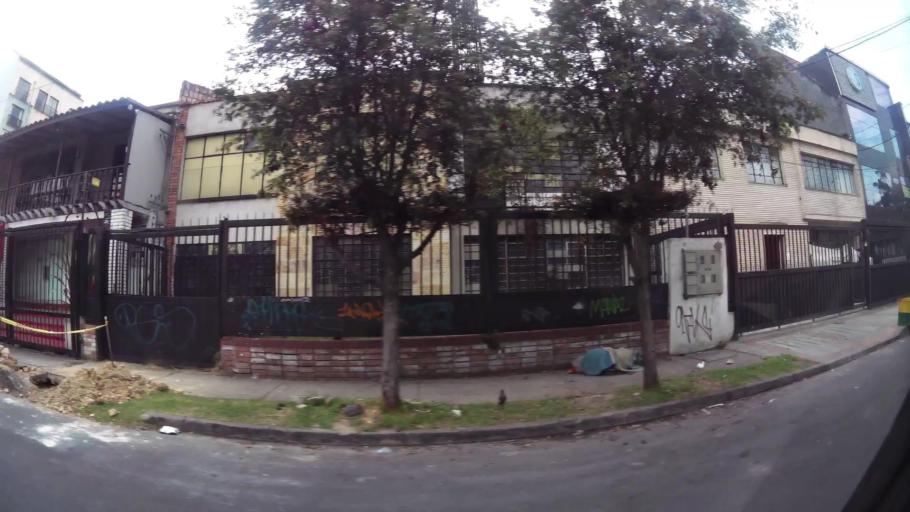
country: CO
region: Bogota D.C.
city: Bogota
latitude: 4.6337
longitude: -74.0790
